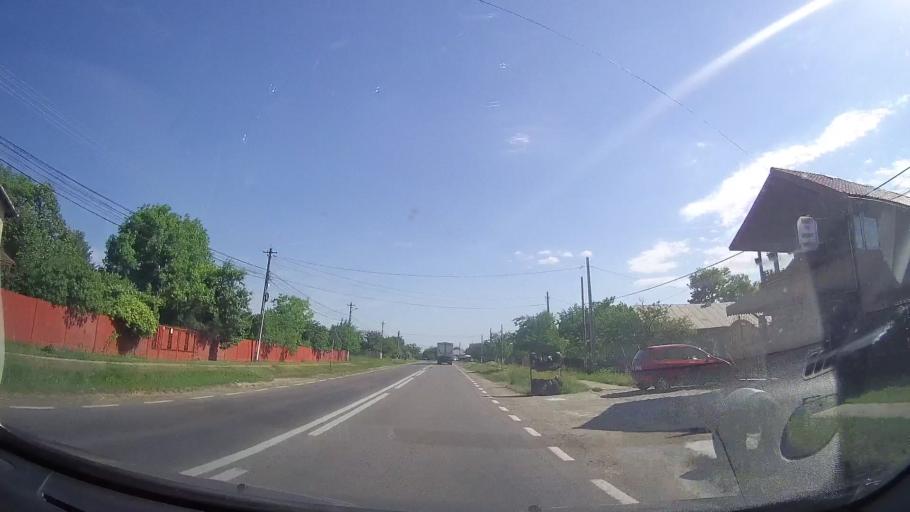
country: RO
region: Prahova
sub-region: Comuna Magurele
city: Magurele
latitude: 45.1200
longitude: 26.0339
